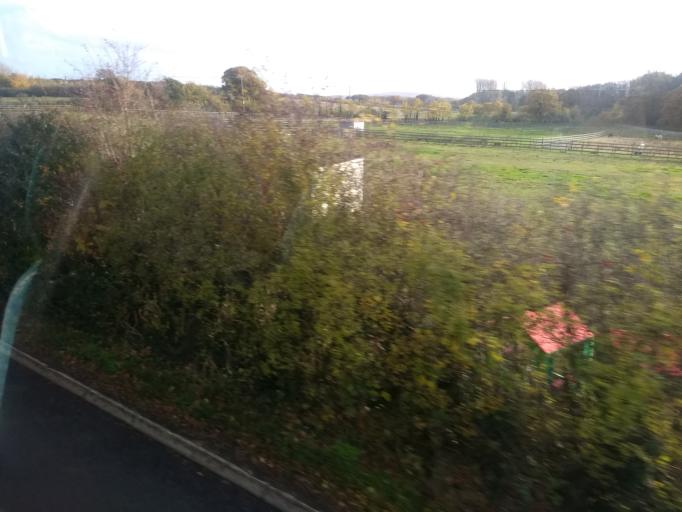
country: GB
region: England
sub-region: Isle of Wight
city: Yarmouth
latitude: 50.7043
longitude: -1.4572
